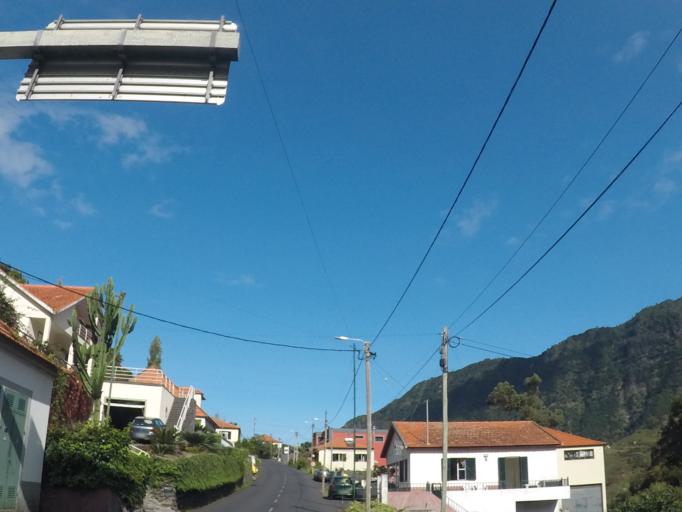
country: PT
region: Madeira
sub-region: Sao Vicente
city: Sao Vicente
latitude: 32.7853
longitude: -17.0332
